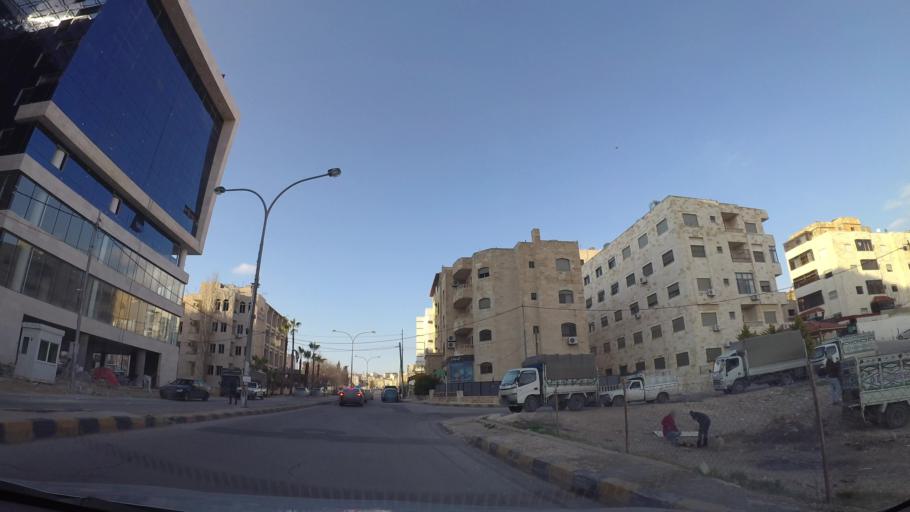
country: JO
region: Amman
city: Al Jubayhah
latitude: 31.9927
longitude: 35.8661
